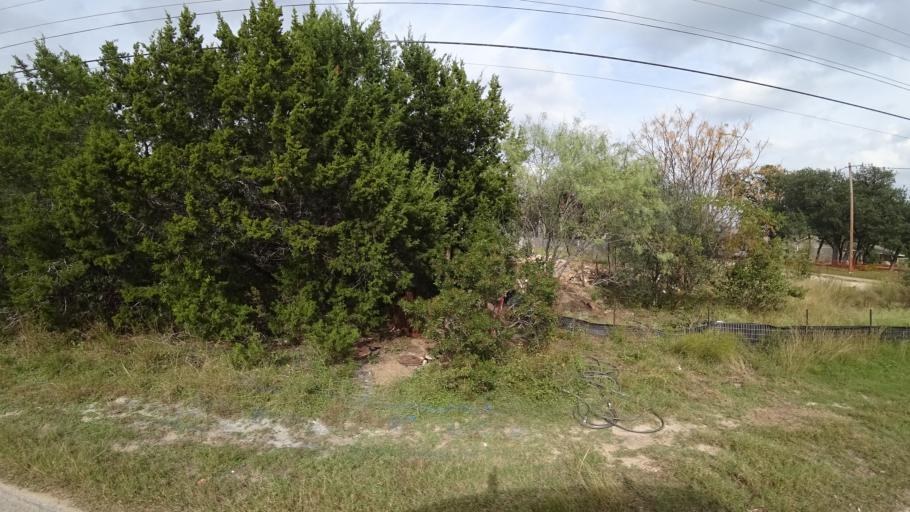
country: US
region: Texas
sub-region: Travis County
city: Hudson Bend
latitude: 30.3818
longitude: -97.9063
